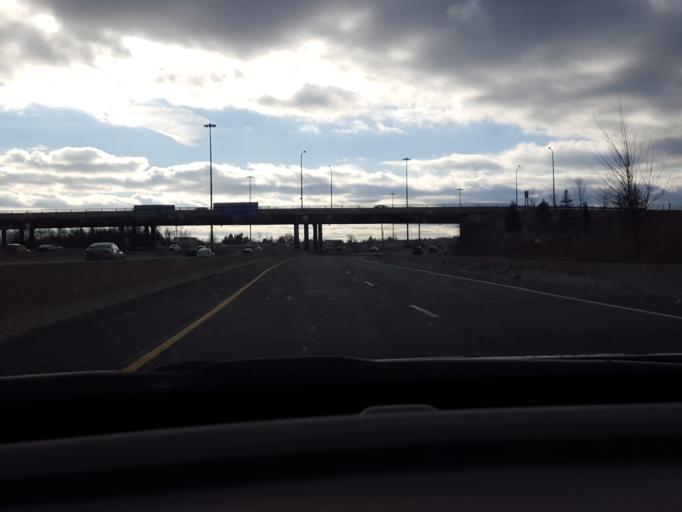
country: CA
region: Ontario
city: Pickering
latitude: 43.7992
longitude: -79.1432
